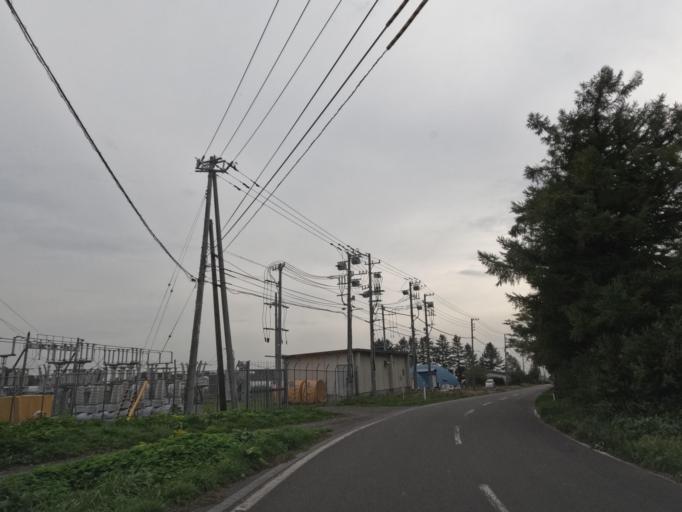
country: JP
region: Hokkaido
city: Date
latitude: 42.4590
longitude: 140.9031
